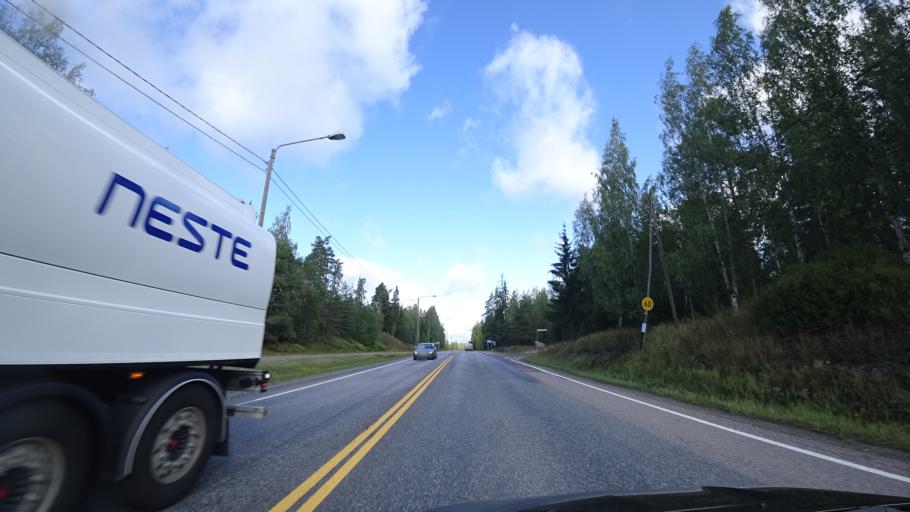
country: FI
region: Uusimaa
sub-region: Helsinki
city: Tuusula
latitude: 60.4391
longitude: 24.9797
